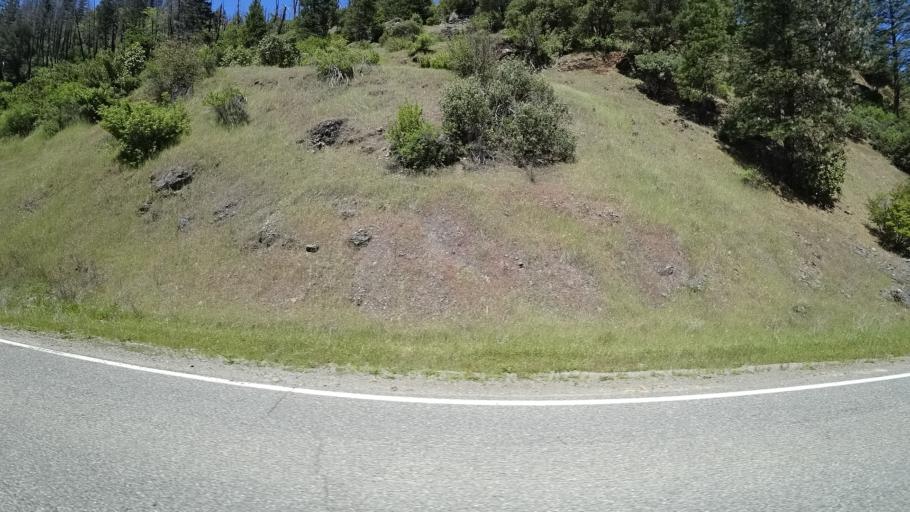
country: US
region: California
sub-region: Trinity County
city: Hayfork
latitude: 40.7777
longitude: -123.3159
